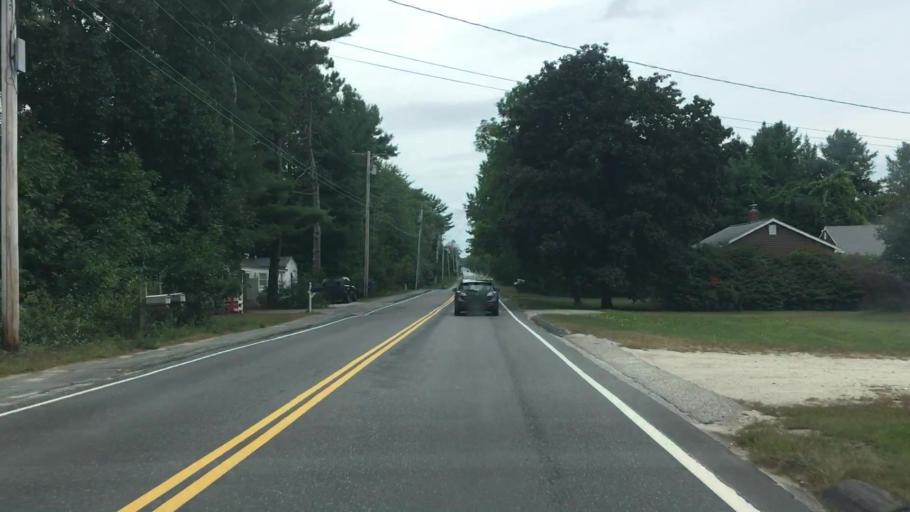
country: US
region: Maine
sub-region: Cumberland County
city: Yarmouth
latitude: 43.8150
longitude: -70.1819
